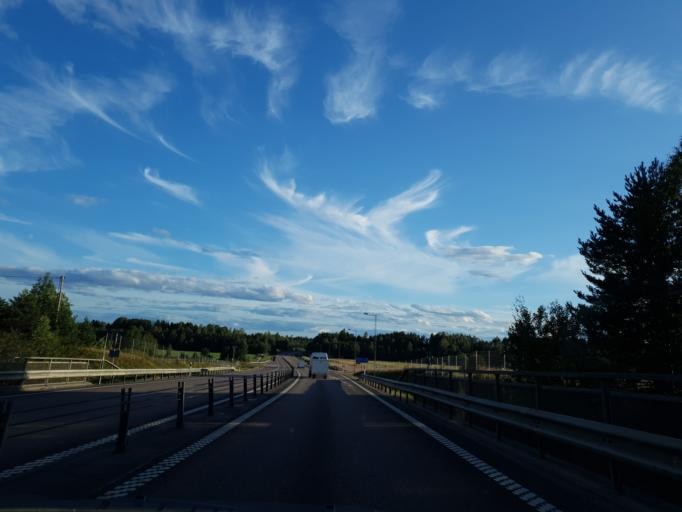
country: SE
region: Gaevleborg
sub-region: Hudiksvalls Kommun
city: Hudiksvall
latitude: 61.7660
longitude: 17.0958
